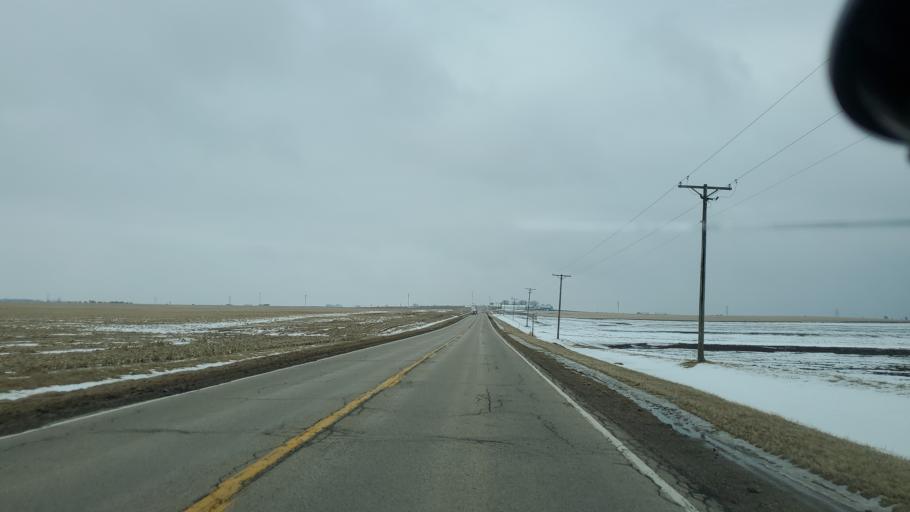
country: US
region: Illinois
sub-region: Marshall County
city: Wenona
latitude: 41.1189
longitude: -89.0913
